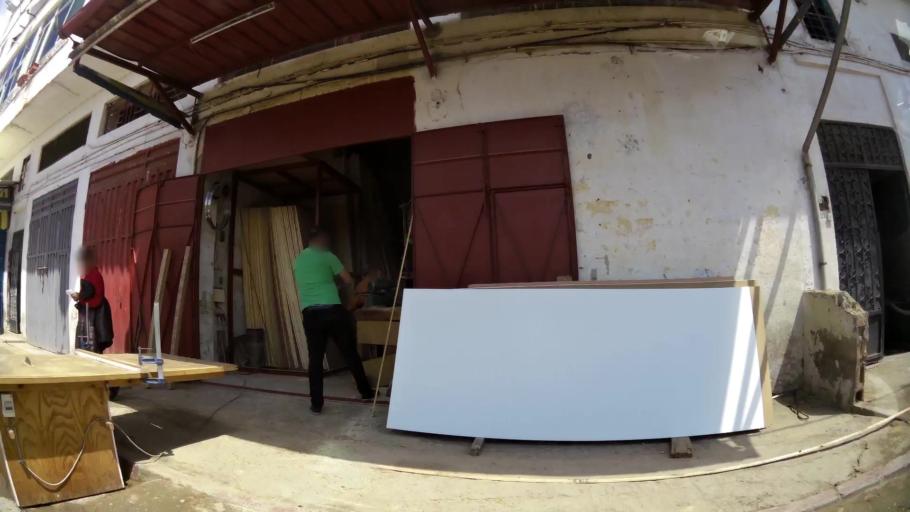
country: MA
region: Grand Casablanca
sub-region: Casablanca
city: Casablanca
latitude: 33.5594
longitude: -7.5964
